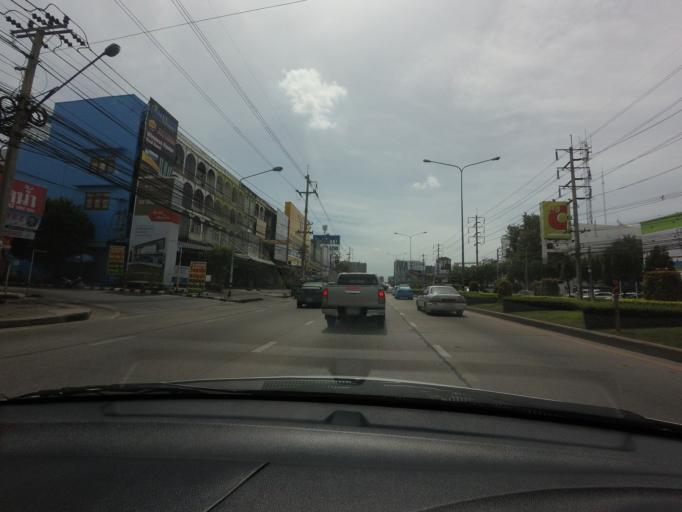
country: TH
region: Bangkok
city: Lak Si
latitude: 13.8933
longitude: 100.5598
